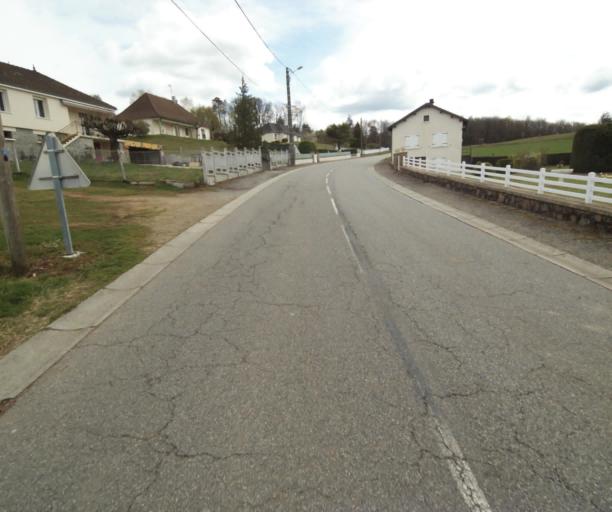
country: FR
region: Limousin
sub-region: Departement de la Correze
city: Laguenne
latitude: 45.2108
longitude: 1.8670
